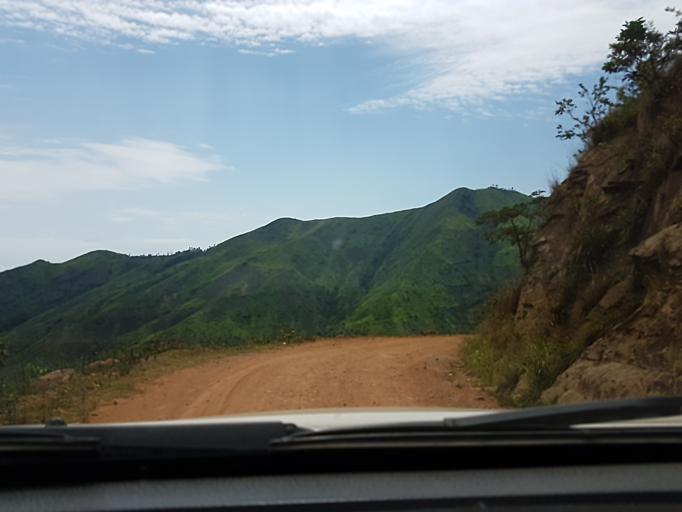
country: RW
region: Western Province
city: Cyangugu
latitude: -2.7055
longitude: 28.9495
